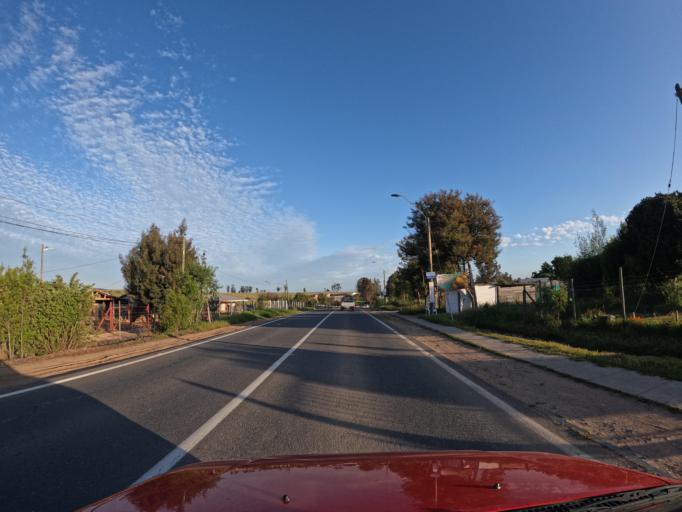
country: CL
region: O'Higgins
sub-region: Provincia de Colchagua
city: Santa Cruz
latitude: -34.2408
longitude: -71.7276
